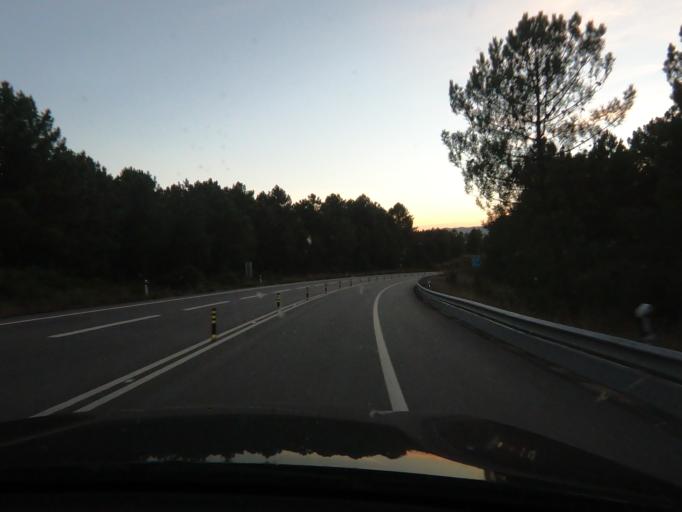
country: PT
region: Vila Real
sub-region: Vila Real
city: Vila Real
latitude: 41.3280
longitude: -7.6790
